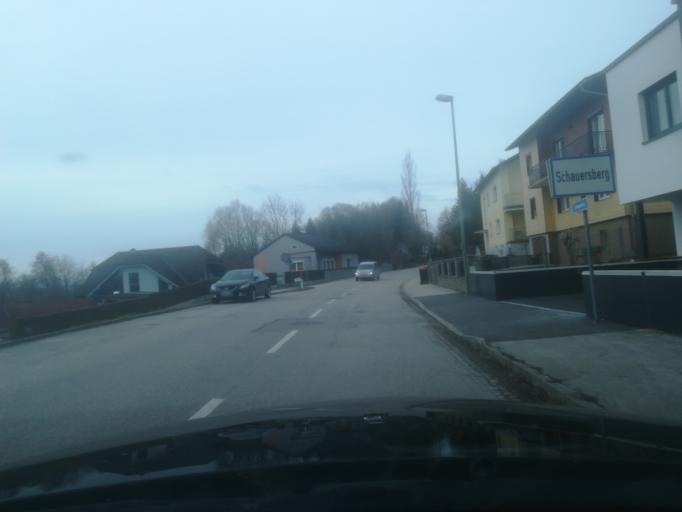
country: AT
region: Upper Austria
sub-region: Wels-Land
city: Steinhaus
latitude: 48.1330
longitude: 14.0091
